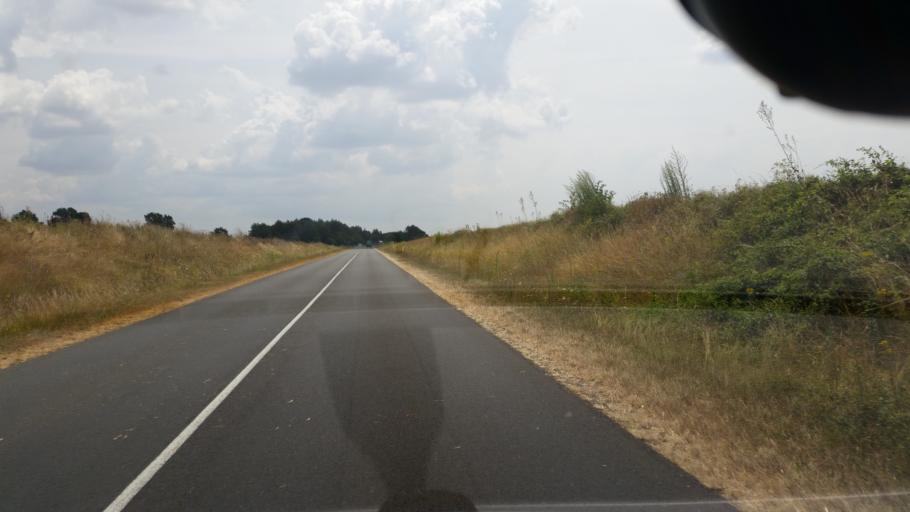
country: FR
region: Poitou-Charentes
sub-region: Departement de la Charente-Maritime
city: Surgeres
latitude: 46.1427
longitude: -0.8013
